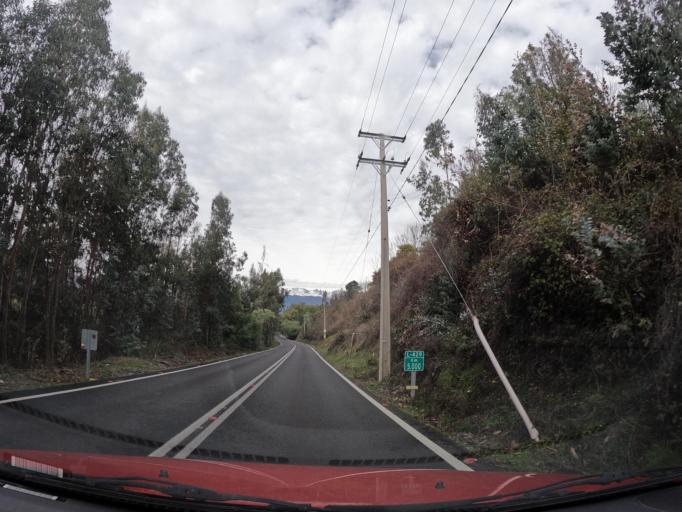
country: CL
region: Maule
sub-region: Provincia de Linares
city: Linares
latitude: -35.9253
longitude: -71.4427
